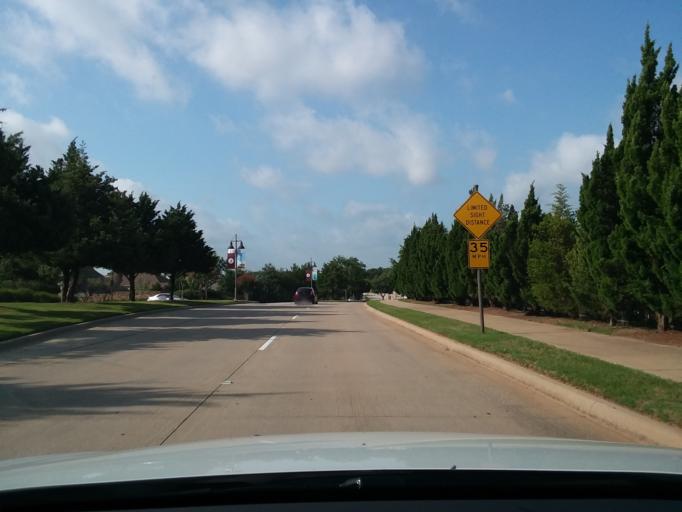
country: US
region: Texas
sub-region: Denton County
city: Bartonville
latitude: 33.0818
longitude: -97.1259
